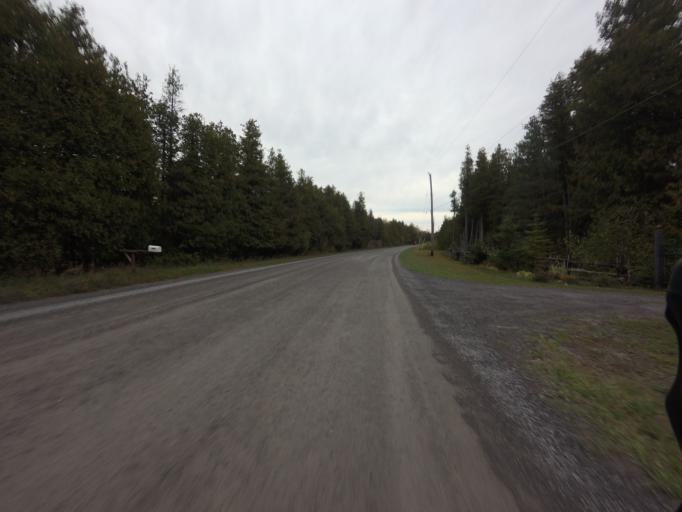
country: CA
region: Ontario
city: Bells Corners
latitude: 45.0676
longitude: -75.7608
